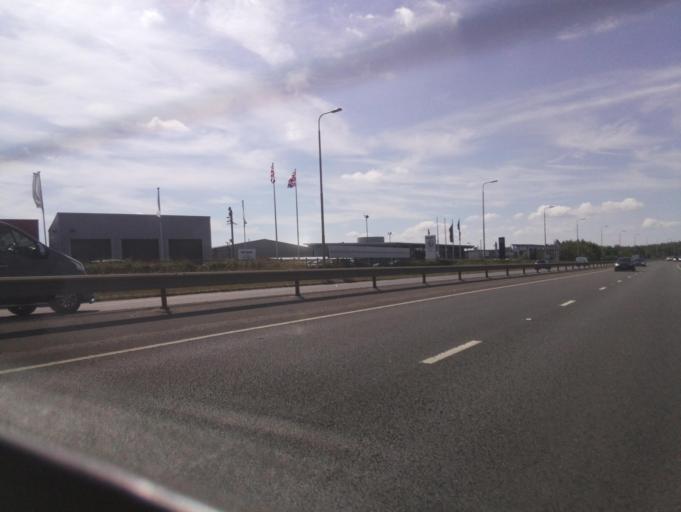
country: GB
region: England
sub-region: Lincolnshire
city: Skellingthorpe
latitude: 53.2052
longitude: -0.6179
